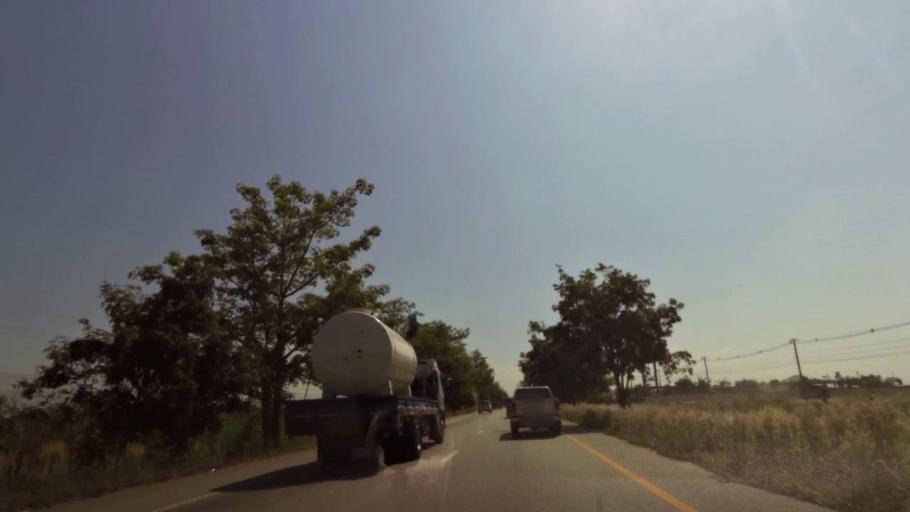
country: TH
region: Nakhon Sawan
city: Kao Liao
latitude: 15.8343
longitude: 100.1180
